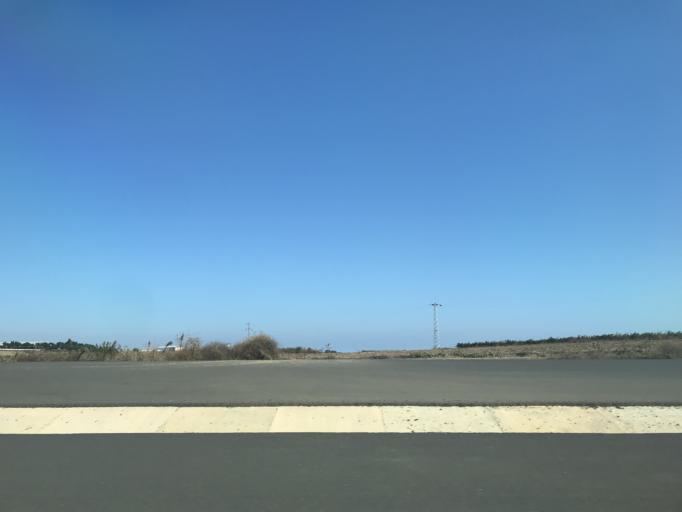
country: TR
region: Tekirdag
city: Kumbag
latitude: 40.9305
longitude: 27.4381
